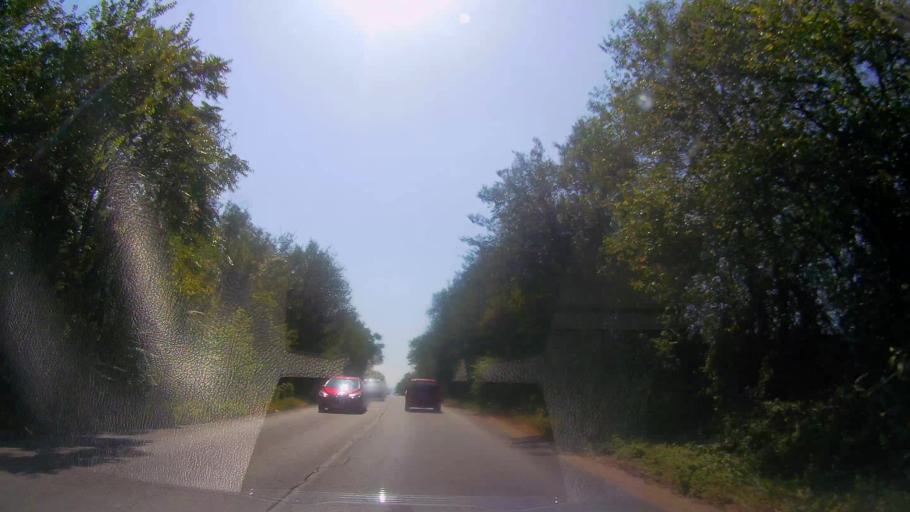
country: BG
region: Veliko Turnovo
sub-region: Obshtina Gorna Oryakhovitsa
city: Purvomaytsi
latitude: 43.2557
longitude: 25.6424
